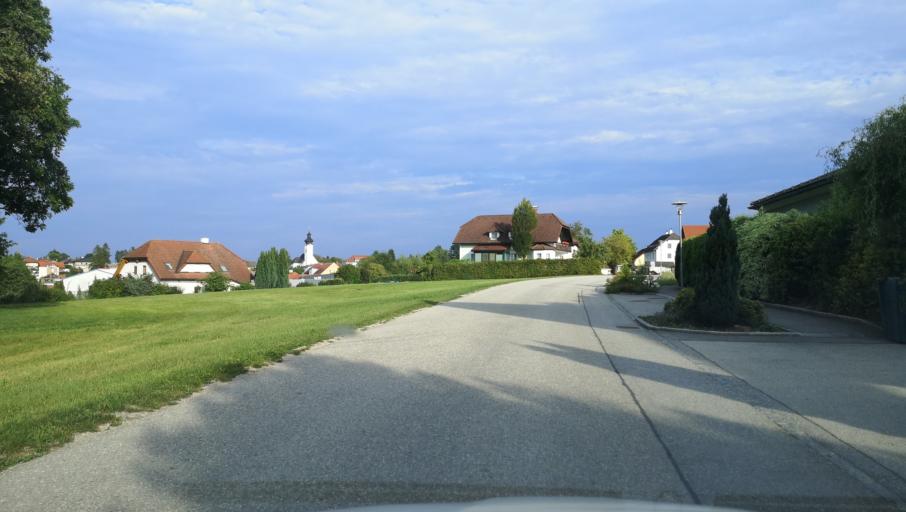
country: AT
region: Lower Austria
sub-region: Politischer Bezirk Amstetten
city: Amstetten
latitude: 48.1515
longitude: 14.8861
